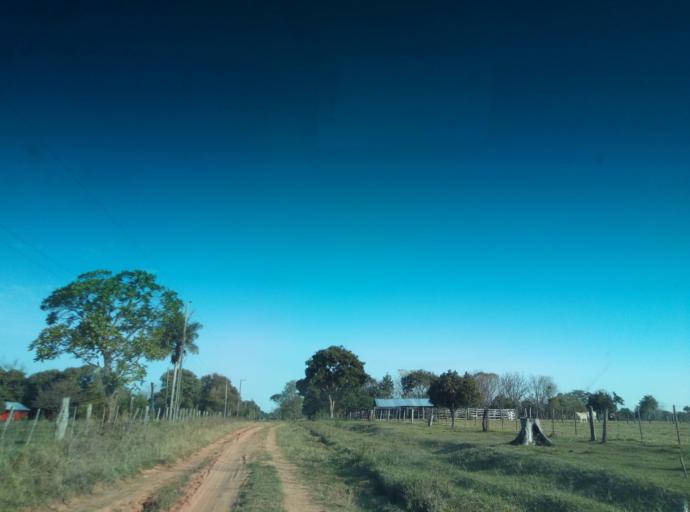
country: PY
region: Caaguazu
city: Doctor Cecilio Baez
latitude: -25.1693
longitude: -56.2321
